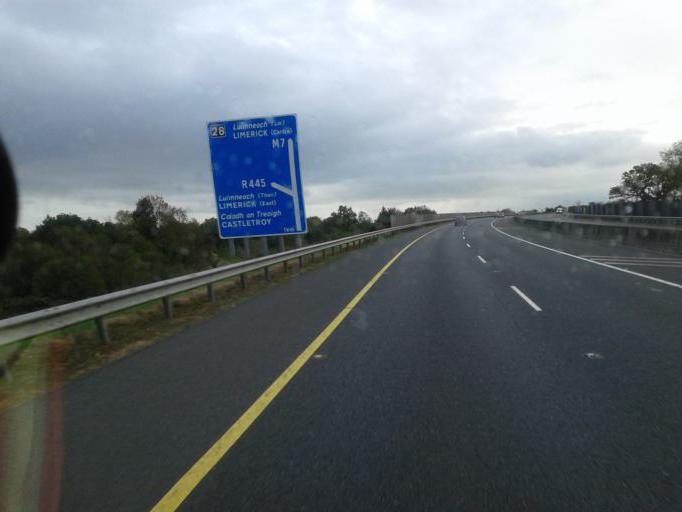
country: IE
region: Munster
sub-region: County Limerick
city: Castleconnell
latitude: 52.6868
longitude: -8.4994
